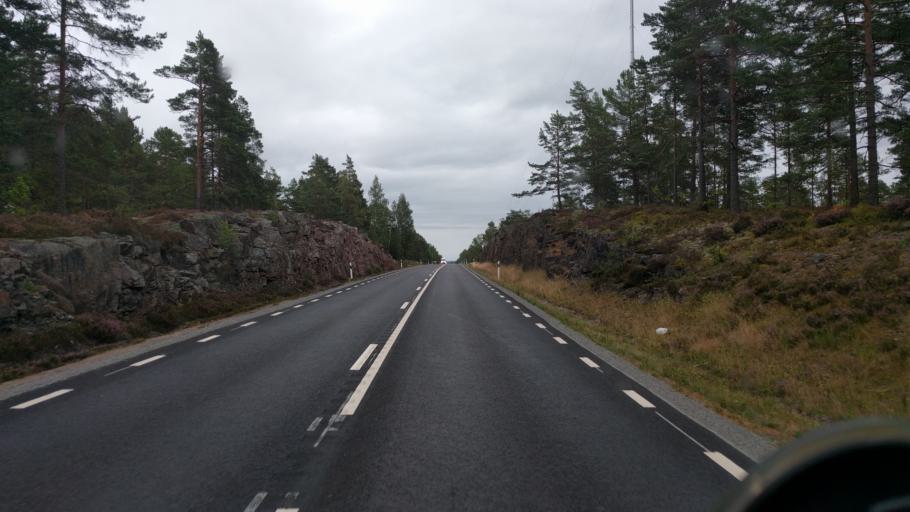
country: SE
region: Kalmar
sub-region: Vasterviks Kommun
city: Ankarsrum
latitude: 57.7233
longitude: 16.4168
